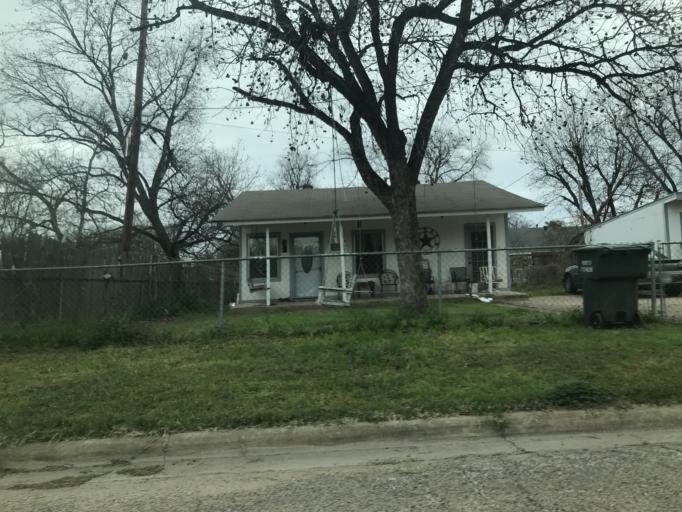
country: US
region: Texas
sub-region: Taylor County
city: Abilene
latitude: 32.4456
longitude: -99.7591
